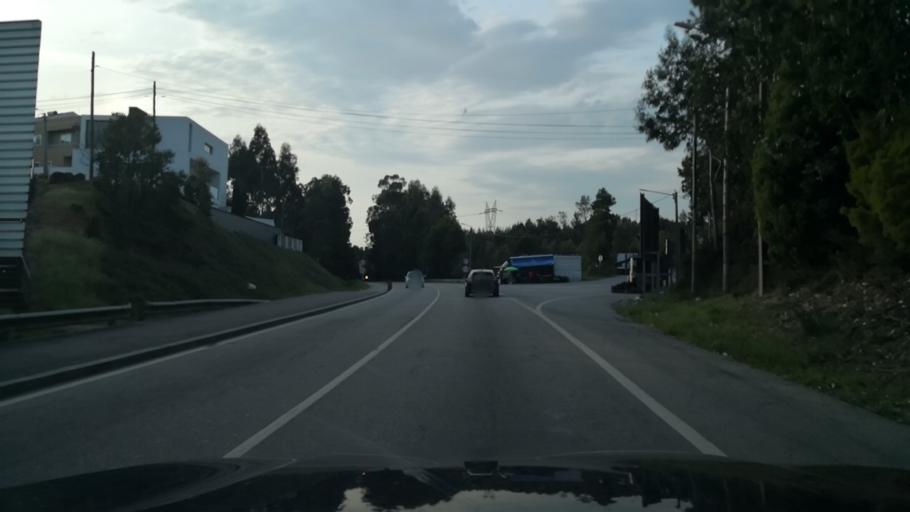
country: PT
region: Porto
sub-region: Valongo
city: Valongo
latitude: 41.1959
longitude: -8.5196
